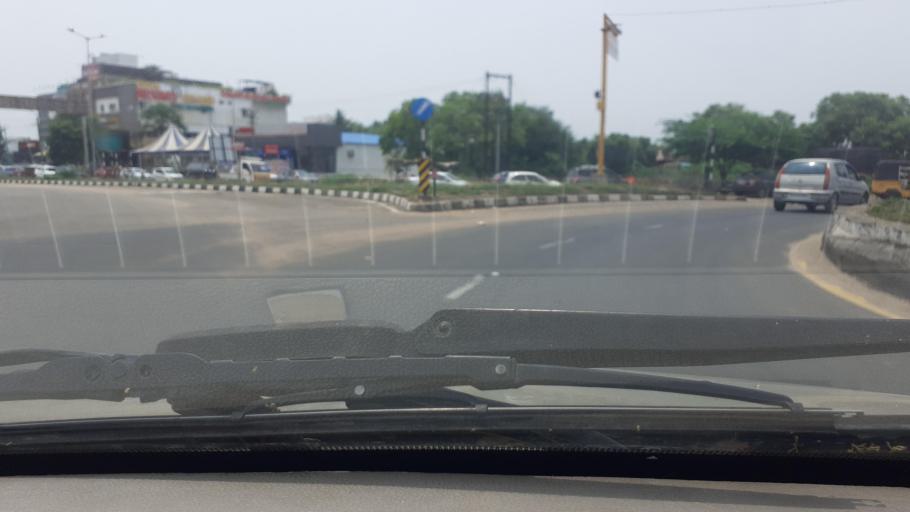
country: IN
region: Tamil Nadu
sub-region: Tirunelveli Kattabo
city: Tirunelveli
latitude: 8.7147
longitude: 77.7648
